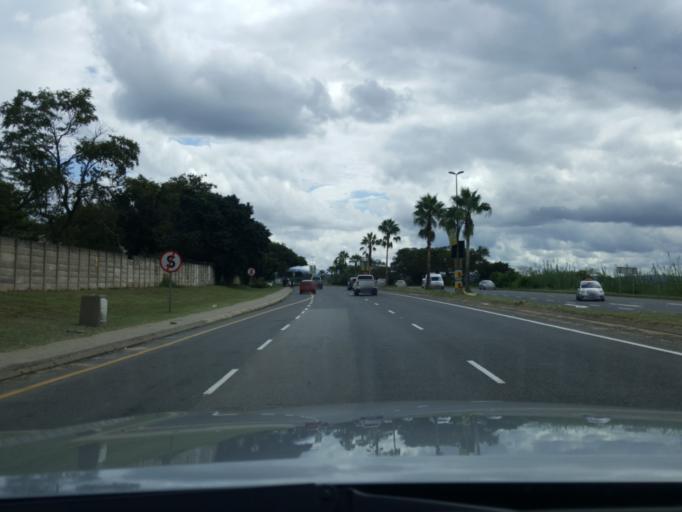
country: ZA
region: Mpumalanga
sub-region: Ehlanzeni District
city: Nelspruit
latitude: -25.4665
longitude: 30.9566
